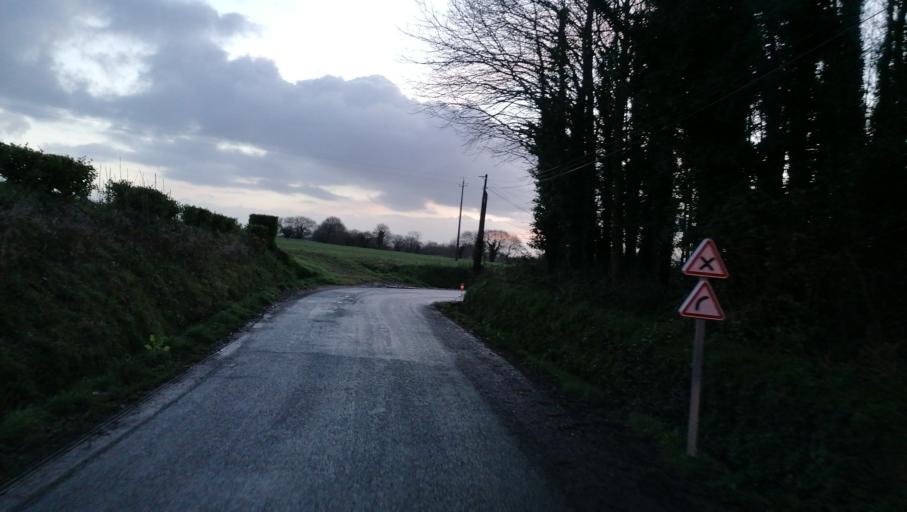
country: FR
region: Brittany
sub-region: Departement des Cotes-d'Armor
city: Plouha
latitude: 48.6680
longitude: -2.9536
